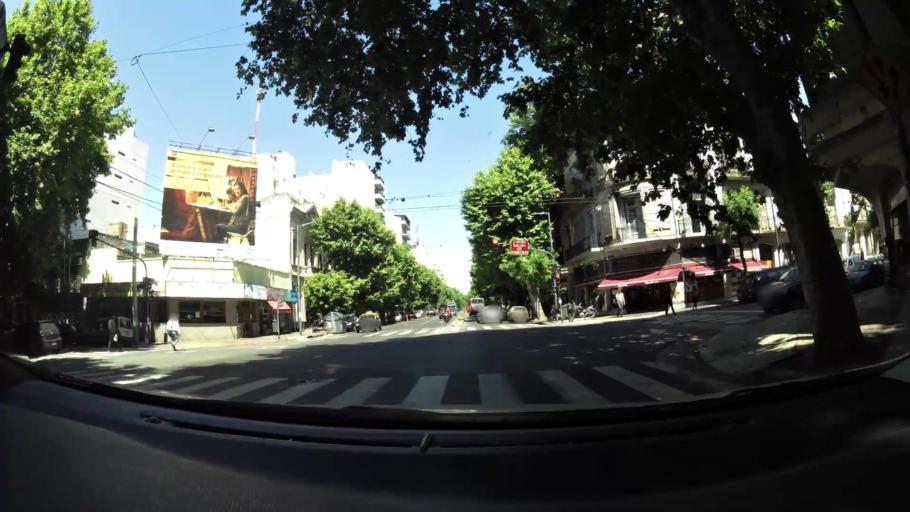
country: AR
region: Buenos Aires F.D.
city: Buenos Aires
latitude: -34.6362
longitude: -58.4004
